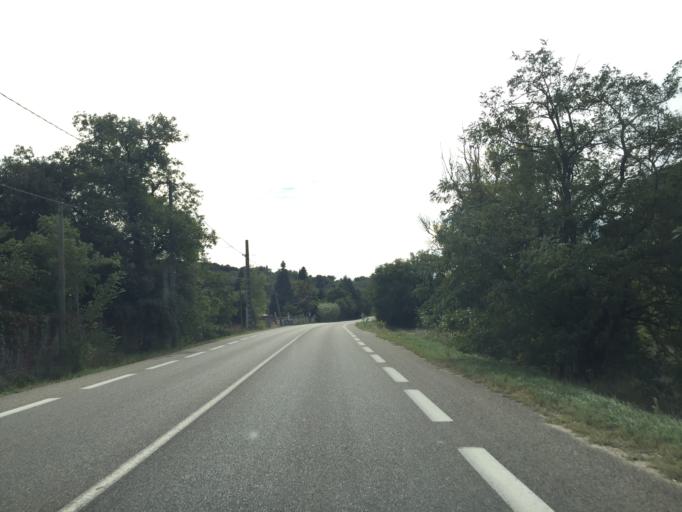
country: FR
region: Provence-Alpes-Cote d'Azur
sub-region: Departement du Vaucluse
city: Bollene
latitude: 44.2593
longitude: 4.7399
